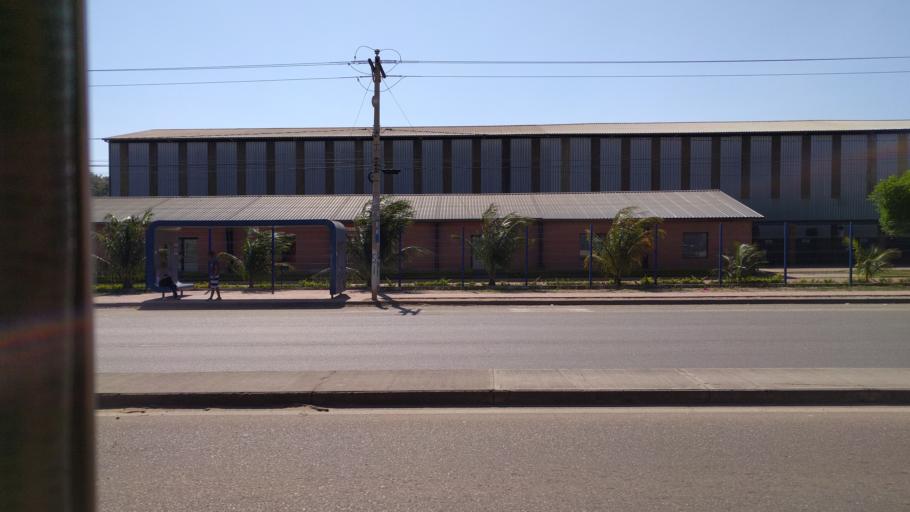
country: BO
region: Santa Cruz
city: Santa Cruz de la Sierra
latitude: -17.7741
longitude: -63.1324
